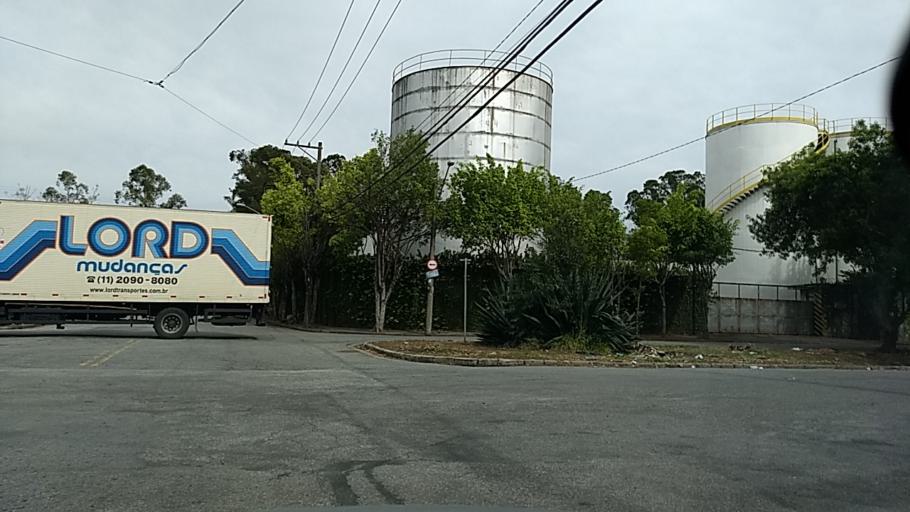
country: BR
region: Sao Paulo
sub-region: Guarulhos
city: Guarulhos
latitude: -23.5014
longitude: -46.5674
